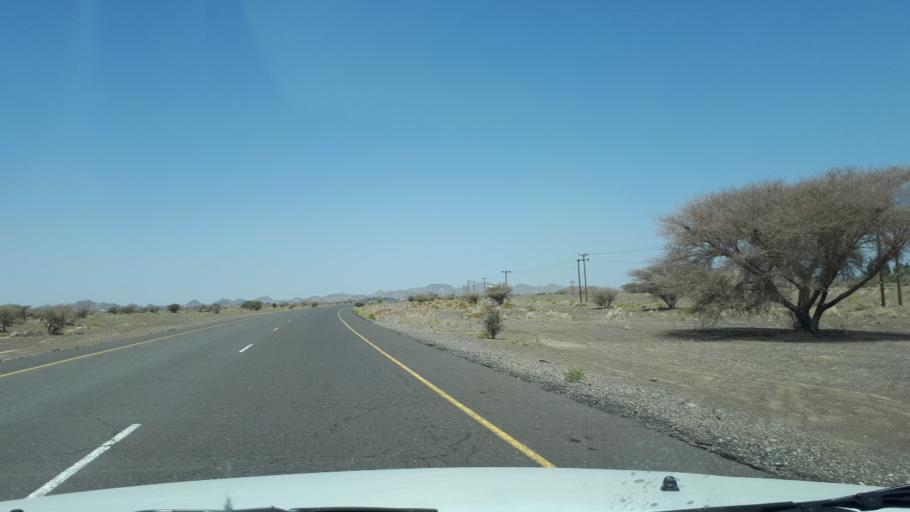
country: OM
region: Ash Sharqiyah
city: Ibra'
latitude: 22.6172
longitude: 58.4215
